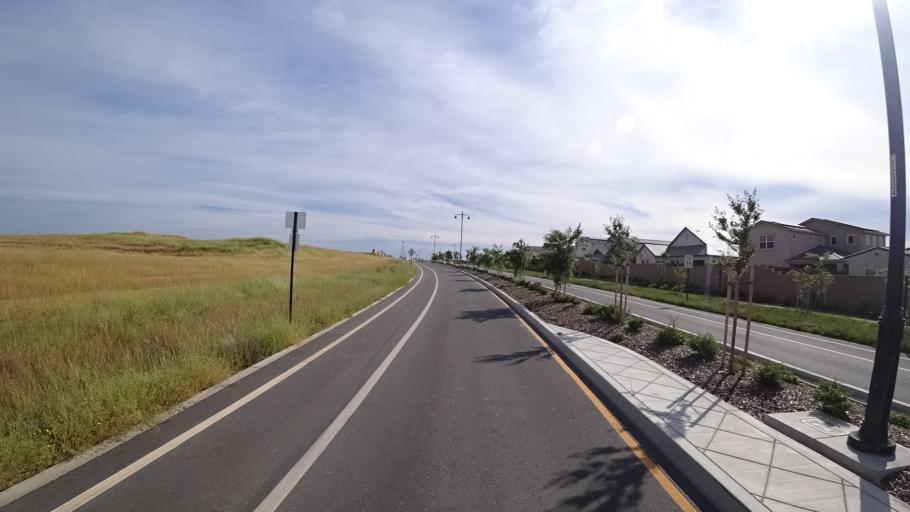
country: US
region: California
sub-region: Placer County
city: Rocklin
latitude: 38.8323
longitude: -121.2661
